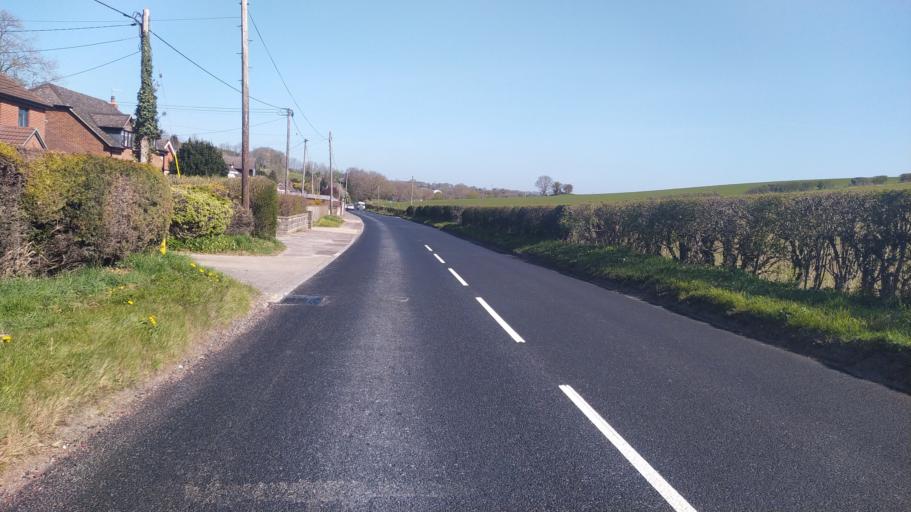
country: GB
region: England
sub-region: Wiltshire
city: Wilton
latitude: 51.0305
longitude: -1.8490
